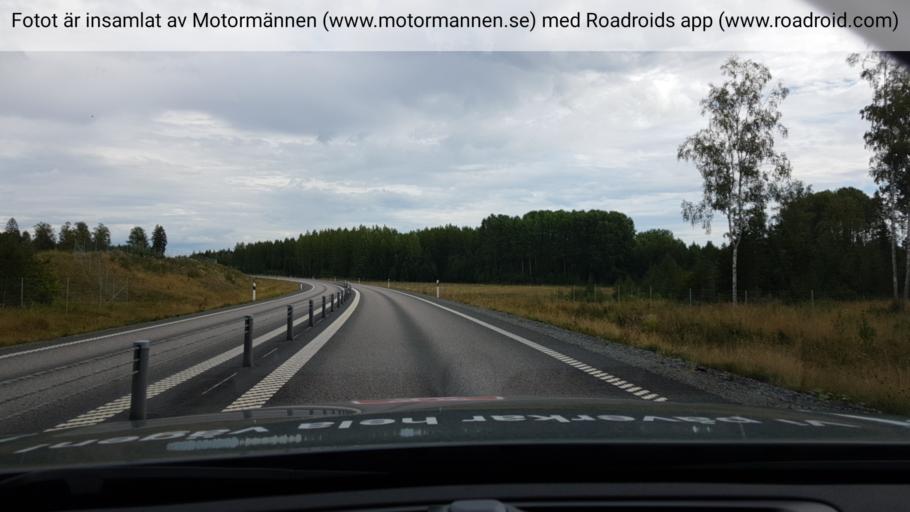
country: SE
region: Uppsala
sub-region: Heby Kommun
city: Heby
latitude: 59.9795
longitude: 16.8518
